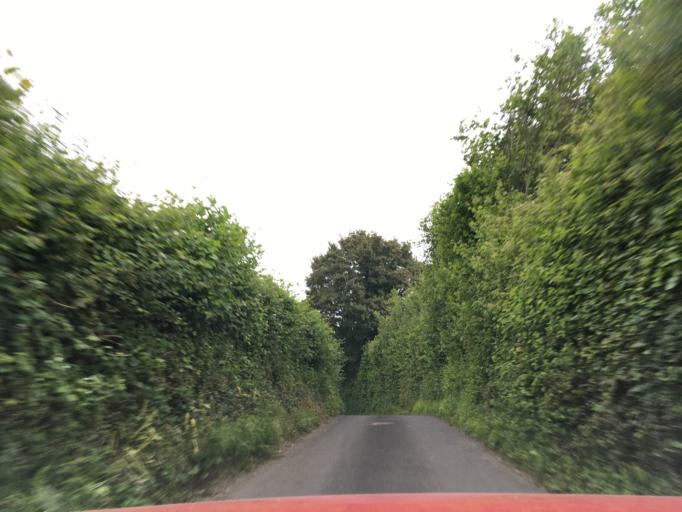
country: GB
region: England
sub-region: North Somerset
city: Dundry
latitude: 51.4020
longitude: -2.6343
